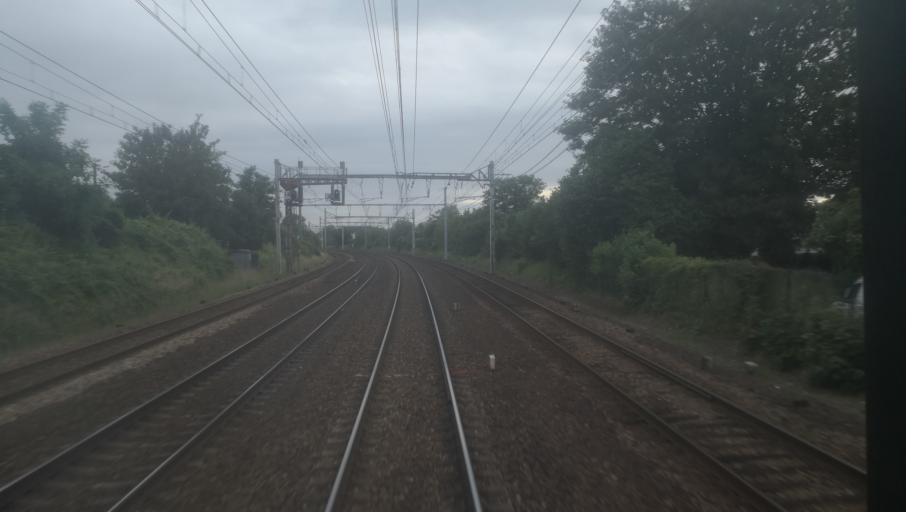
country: FR
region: Ile-de-France
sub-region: Departement de l'Essonne
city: Bouray-sur-Juine
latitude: 48.5340
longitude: 2.2912
